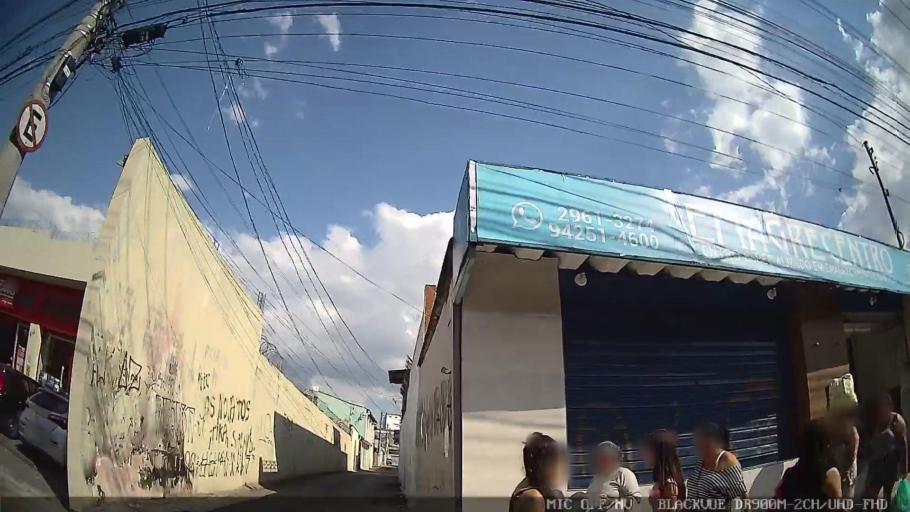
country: BR
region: Sao Paulo
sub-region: Ferraz De Vasconcelos
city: Ferraz de Vasconcelos
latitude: -23.5368
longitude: -46.4043
